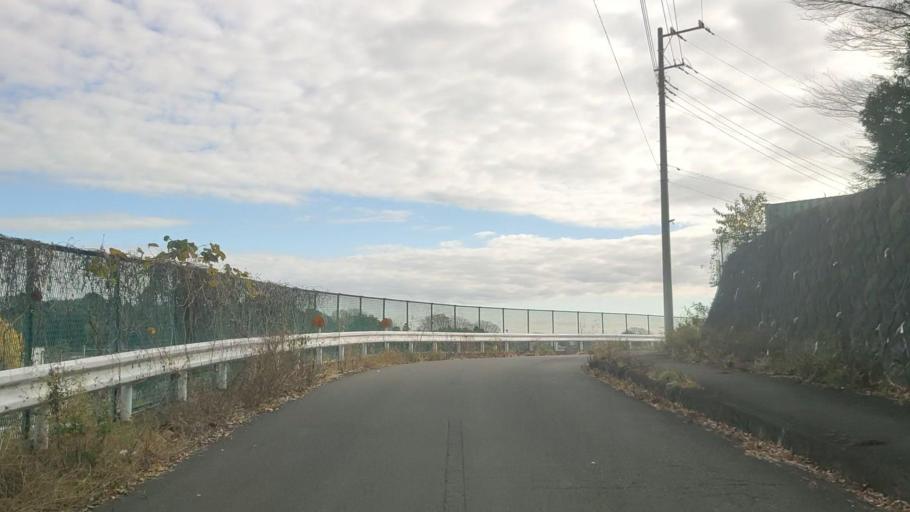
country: JP
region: Kanagawa
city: Minami-rinkan
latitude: 35.4857
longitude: 139.4689
